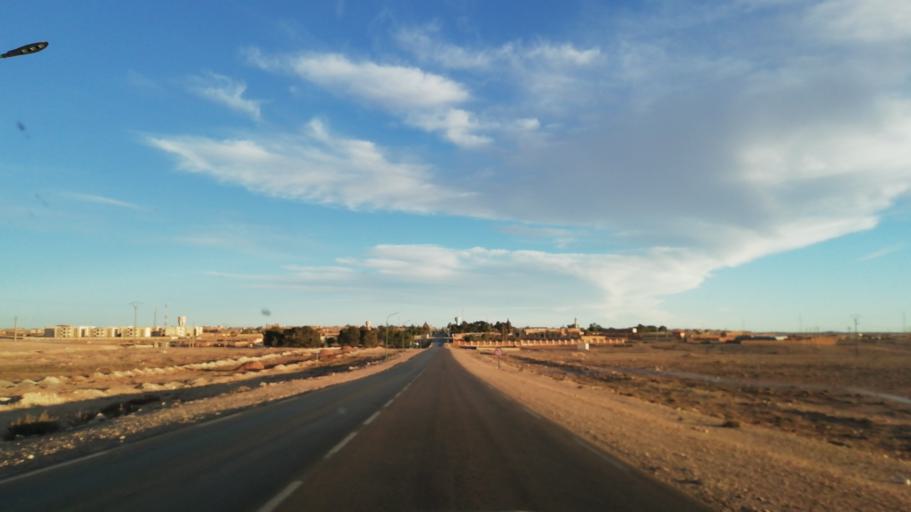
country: DZ
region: Wilaya de Naama
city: Naama
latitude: 33.7226
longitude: -0.7372
